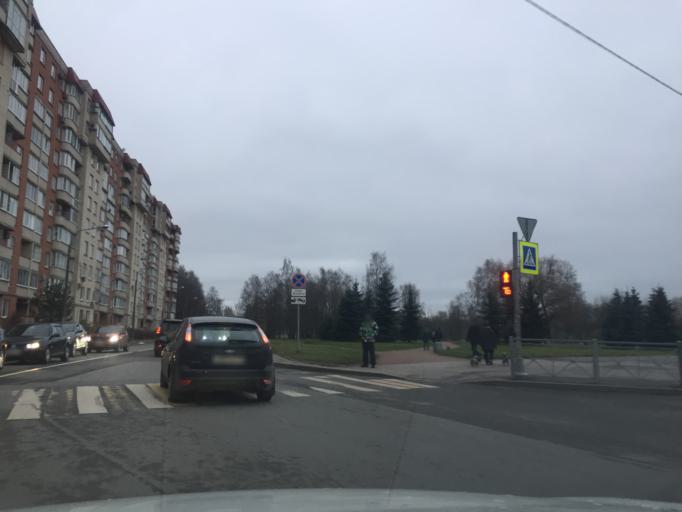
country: RU
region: Leningrad
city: Akademicheskoe
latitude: 60.0212
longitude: 30.3735
